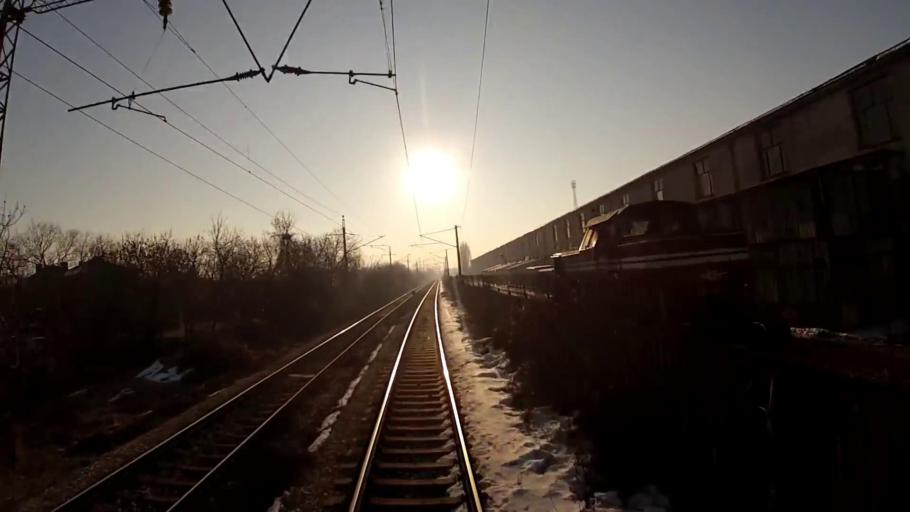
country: BG
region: Sofia-Capital
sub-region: Stolichna Obshtina
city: Sofia
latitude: 42.7284
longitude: 23.2813
